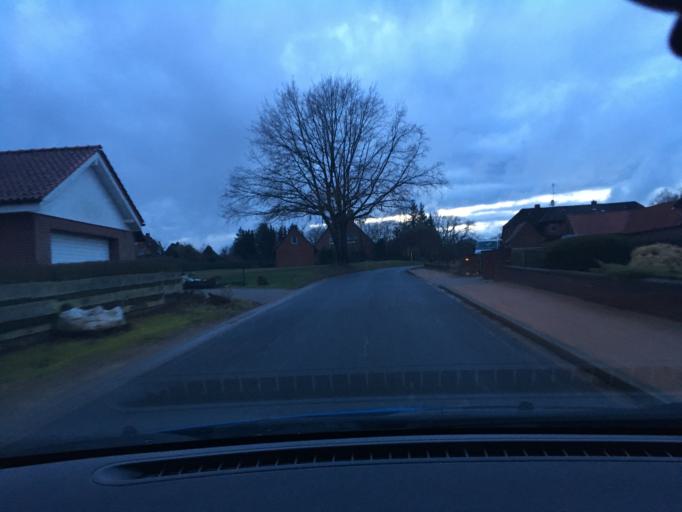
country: DE
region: Lower Saxony
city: Betzendorf
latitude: 53.1363
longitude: 10.3171
